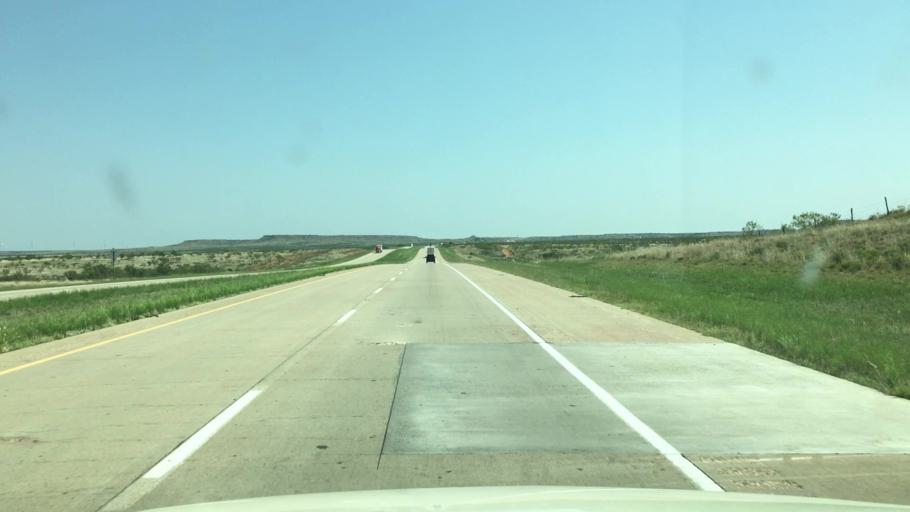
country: US
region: Texas
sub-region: Oldham County
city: Vega
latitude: 35.2323
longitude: -102.8504
